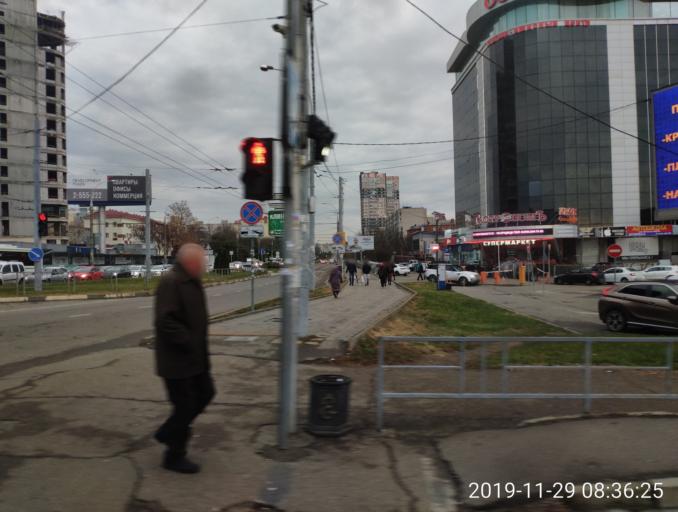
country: RU
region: Krasnodarskiy
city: Krasnodar
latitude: 45.0550
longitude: 39.0026
